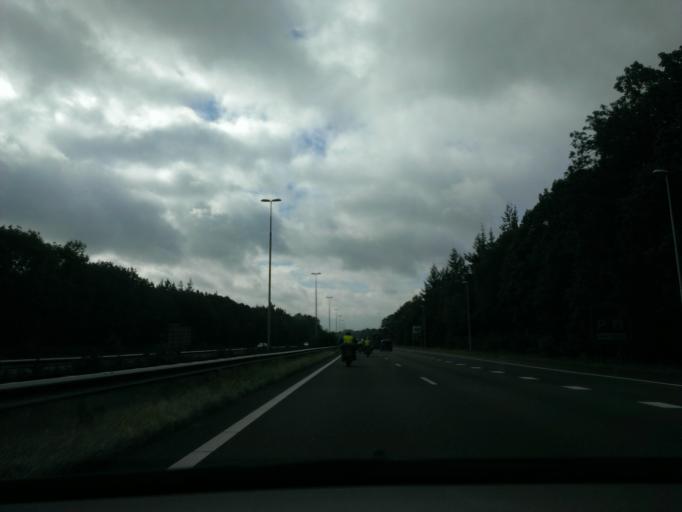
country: NL
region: Gelderland
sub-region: Gemeente Heerde
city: Heerde
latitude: 52.4004
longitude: 6.0147
